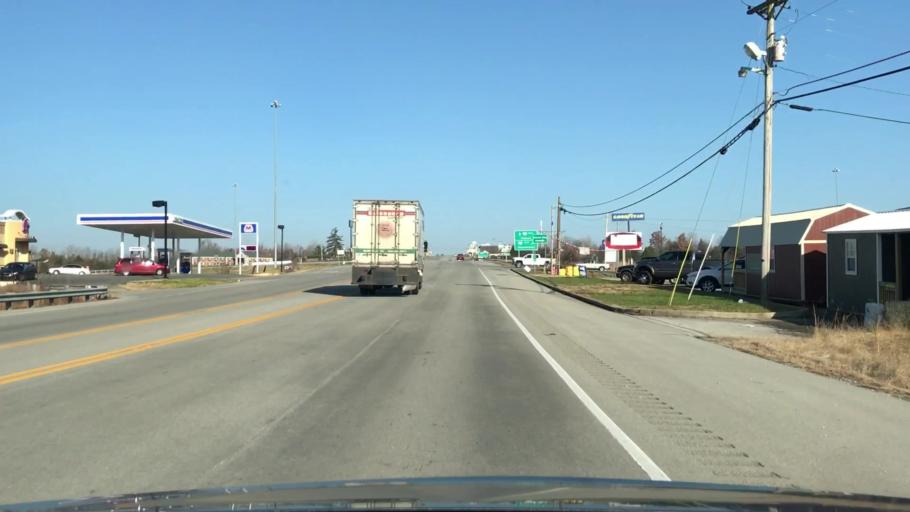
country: US
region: Kentucky
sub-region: Grayson County
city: Leitchfield
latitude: 37.4639
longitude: -86.2913
